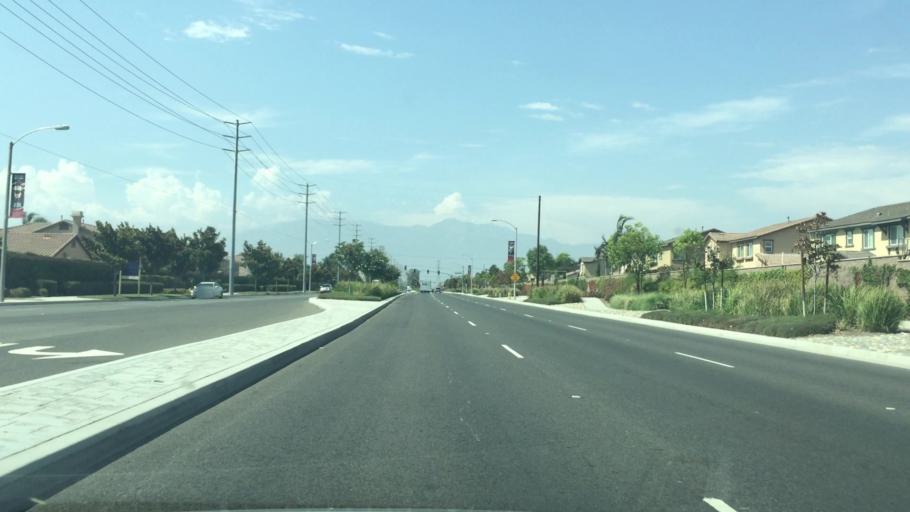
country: US
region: California
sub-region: Riverside County
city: Norco
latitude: 33.9618
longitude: -117.5930
